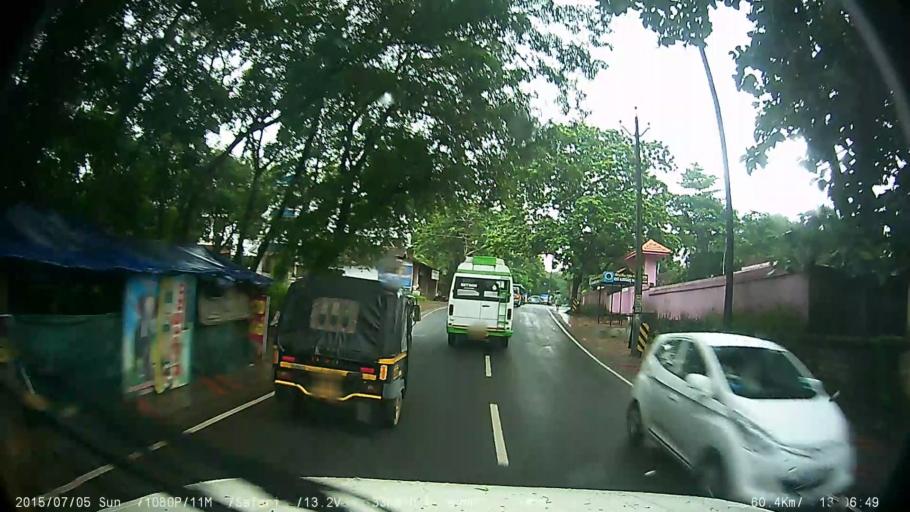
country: IN
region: Kerala
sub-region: Kottayam
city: Changanacheri
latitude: 9.5164
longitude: 76.5724
